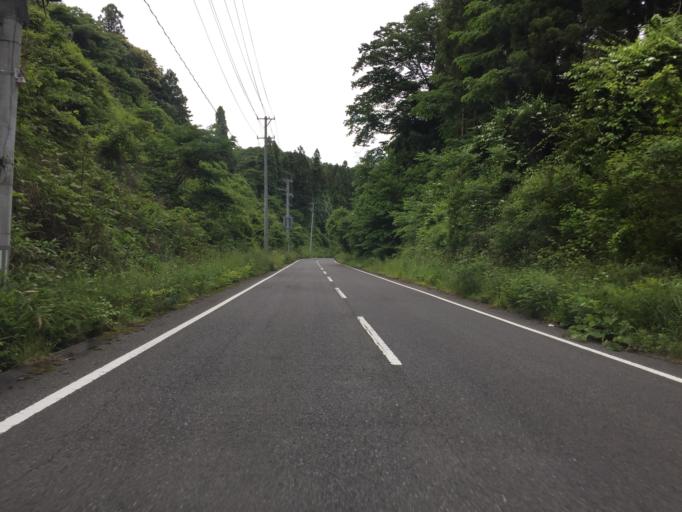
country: JP
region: Fukushima
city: Funehikimachi-funehiki
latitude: 37.4104
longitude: 140.6482
